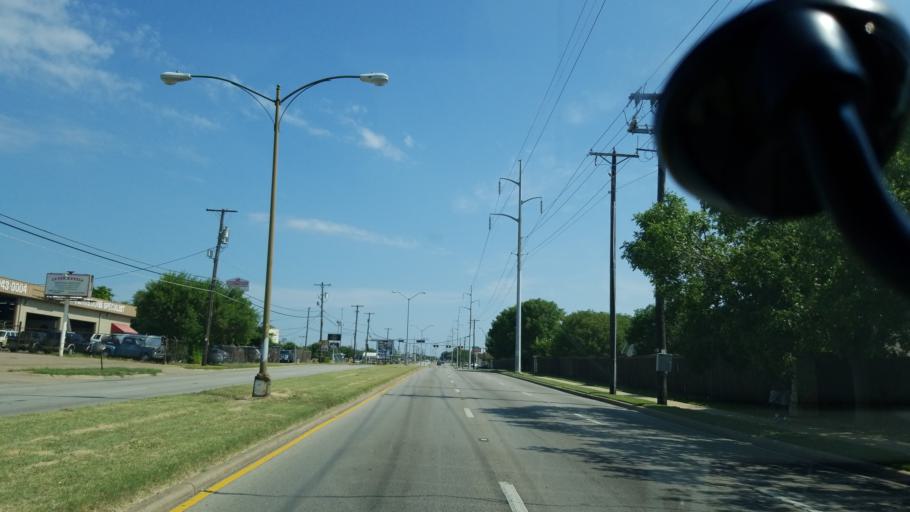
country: US
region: Texas
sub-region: Dallas County
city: Cockrell Hill
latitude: 32.7115
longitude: -96.8743
